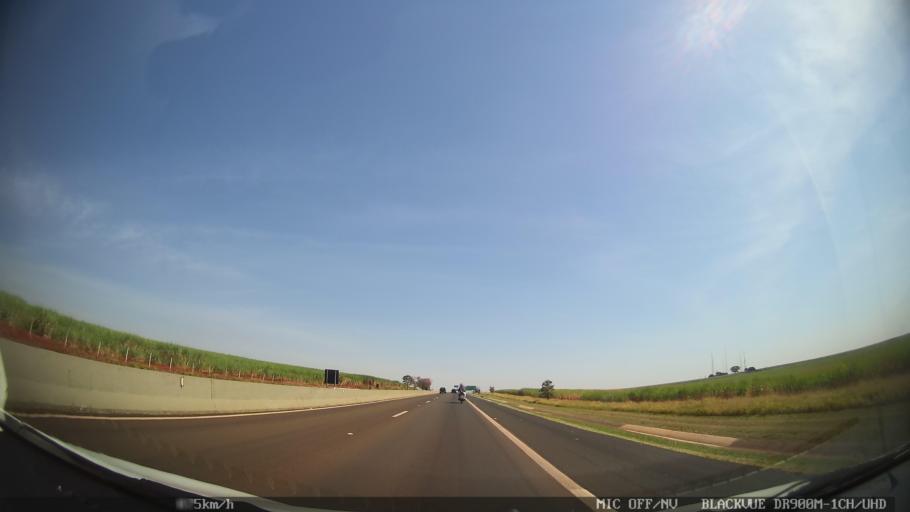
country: BR
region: Sao Paulo
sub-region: Ribeirao Preto
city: Ribeirao Preto
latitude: -21.1661
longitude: -47.8886
